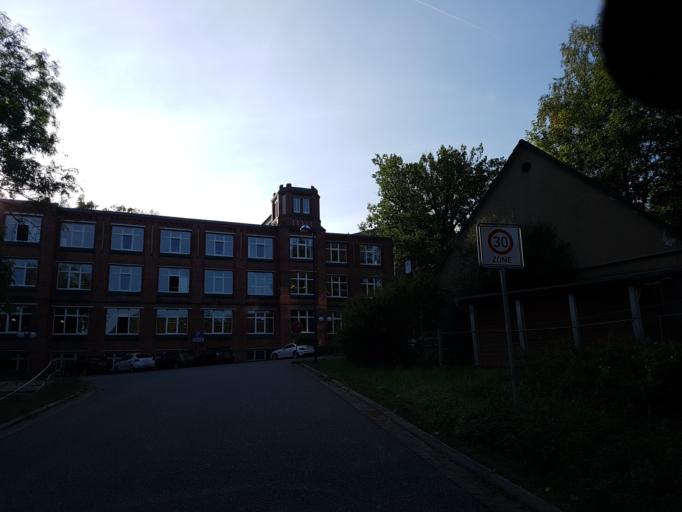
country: DE
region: Saxony
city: Waldheim
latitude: 51.0767
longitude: 13.0211
